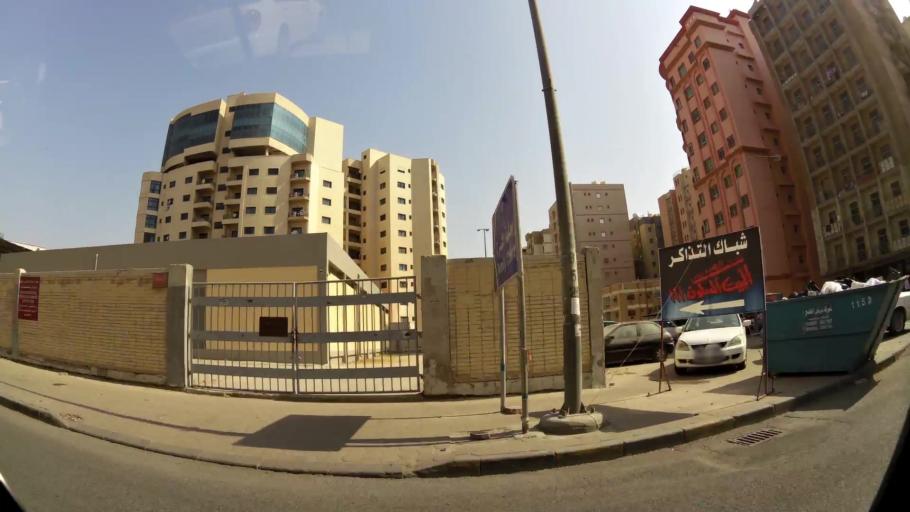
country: KW
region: Muhafazat Hawalli
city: Hawalli
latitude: 29.3382
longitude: 48.0306
